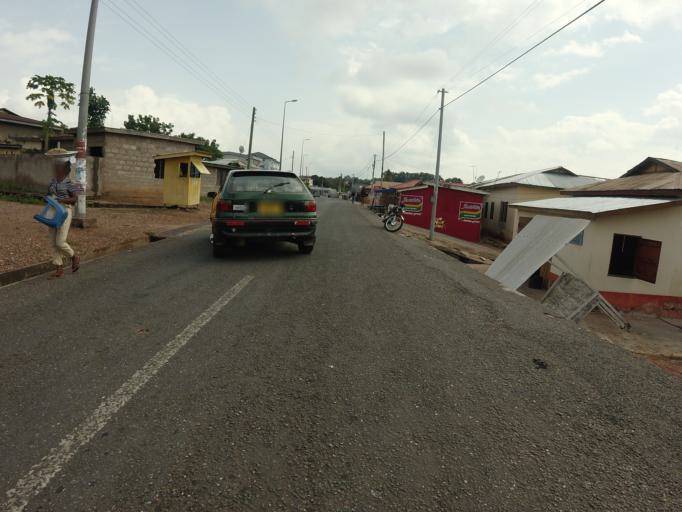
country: GH
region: Volta
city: Ho
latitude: 6.6100
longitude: 0.4727
